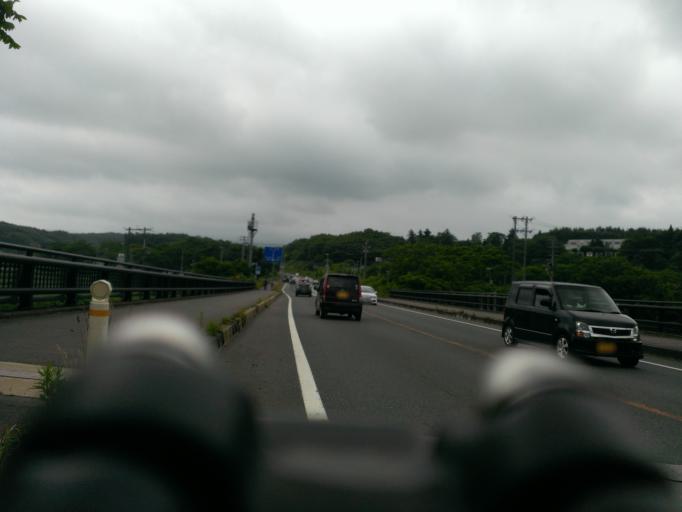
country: JP
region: Iwate
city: Morioka-shi
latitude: 39.8351
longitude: 141.1610
